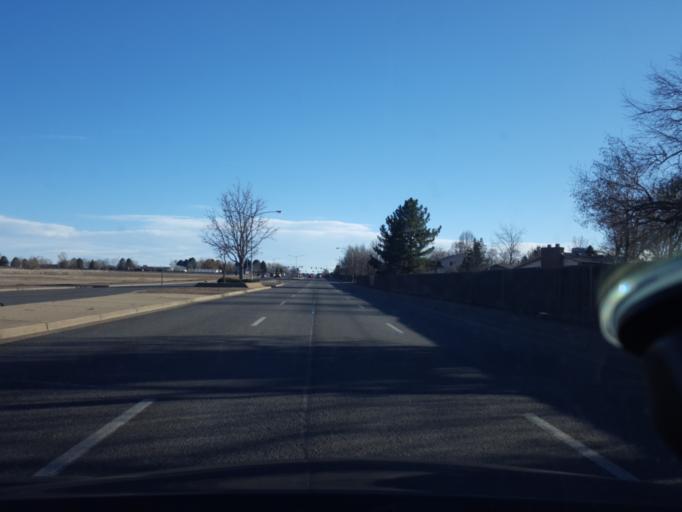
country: US
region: Colorado
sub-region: Adams County
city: Aurora
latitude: 39.7296
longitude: -104.7913
